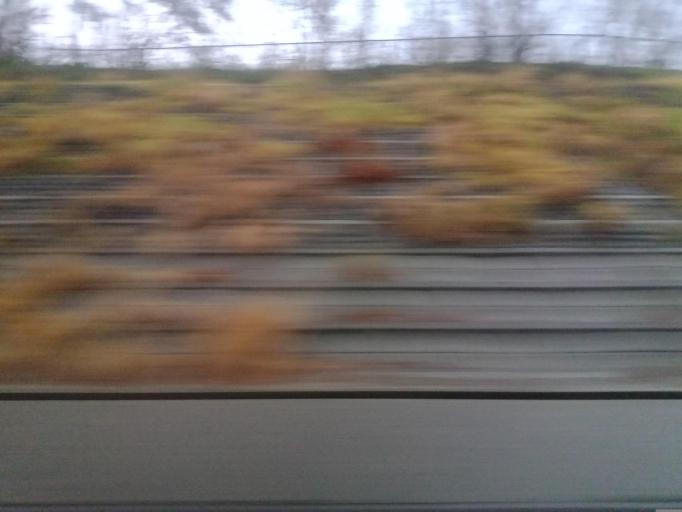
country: JP
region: Niigata
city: Joetsu
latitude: 37.2374
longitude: 138.3469
